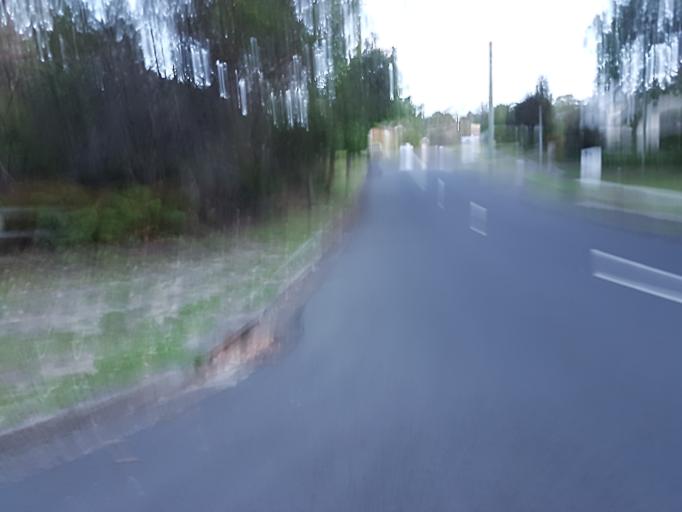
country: AU
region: New South Wales
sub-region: Warringah
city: Davidson
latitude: -33.7461
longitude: 151.2108
